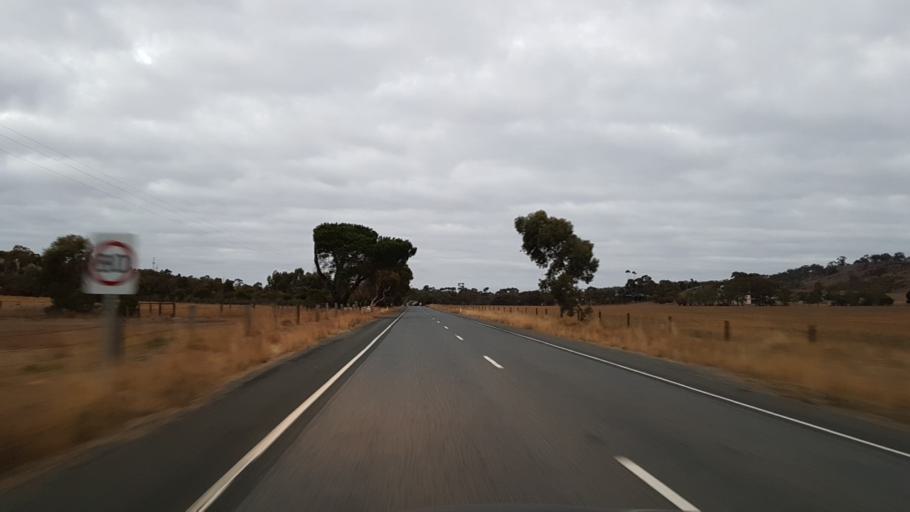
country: AU
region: South Australia
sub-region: Mount Barker
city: Callington
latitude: -35.0629
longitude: 139.0121
